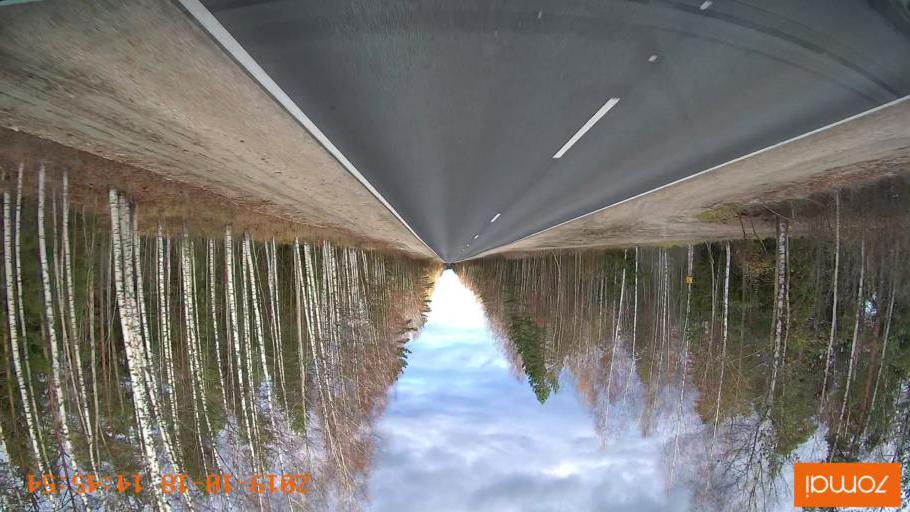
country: RU
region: Vladimir
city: Velikodvorskiy
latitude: 55.3624
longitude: 40.6798
